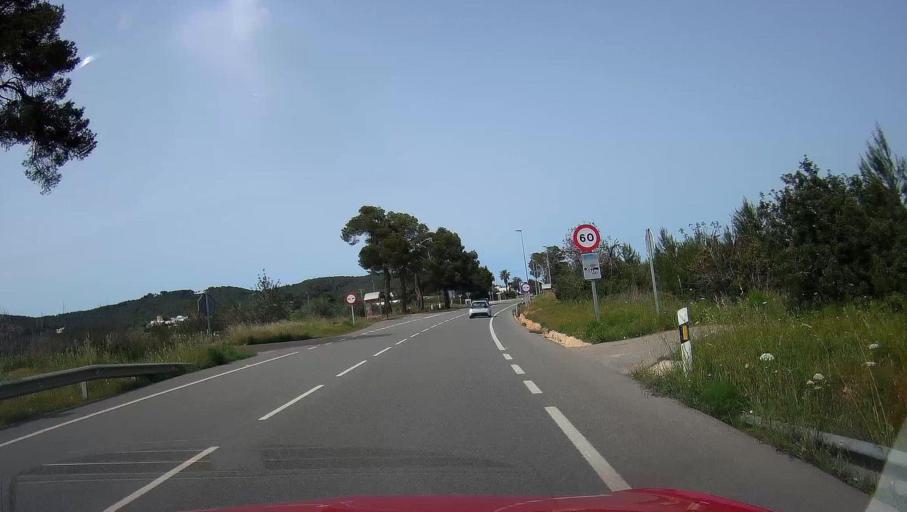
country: ES
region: Balearic Islands
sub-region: Illes Balears
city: Sant Joan de Labritja
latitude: 39.0255
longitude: 1.4871
